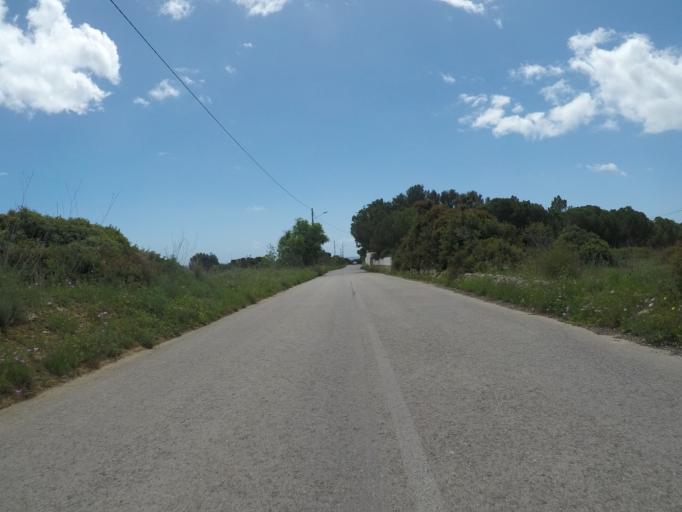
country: PT
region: Faro
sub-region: Lagoa
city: Carvoeiro
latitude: 37.0943
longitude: -8.4195
